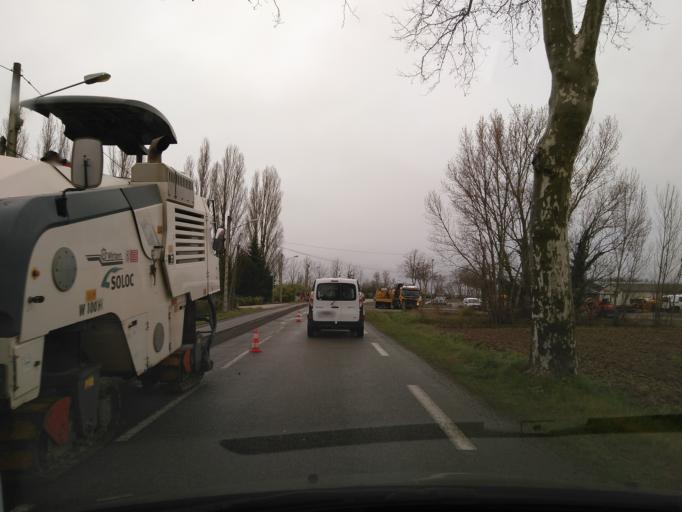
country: FR
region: Midi-Pyrenees
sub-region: Departement de la Haute-Garonne
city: Rieux-Volvestre
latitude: 43.2645
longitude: 1.1942
